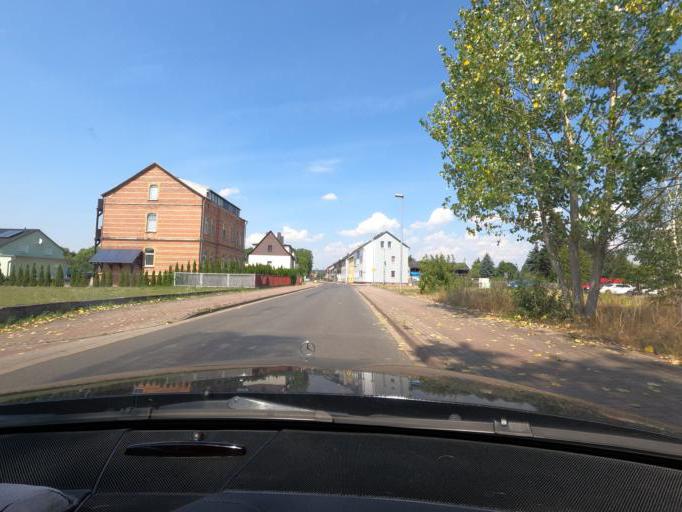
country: DE
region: Thuringia
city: Nordhausen
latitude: 51.5111
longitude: 10.7718
